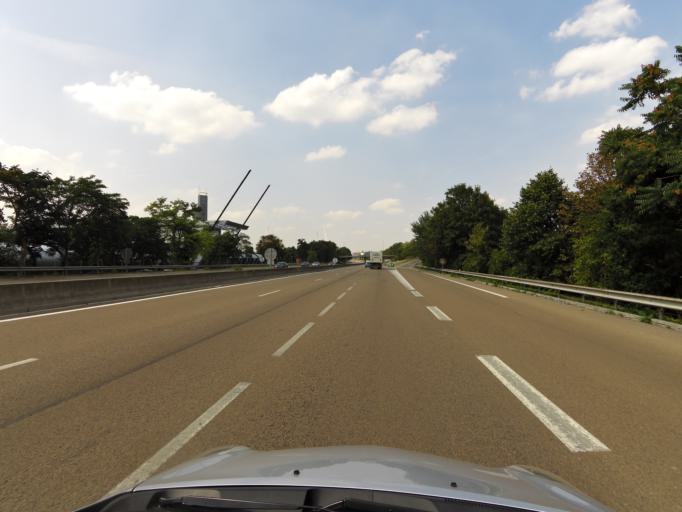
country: FR
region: Champagne-Ardenne
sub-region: Departement de la Marne
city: Reims
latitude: 49.2428
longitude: 4.0314
